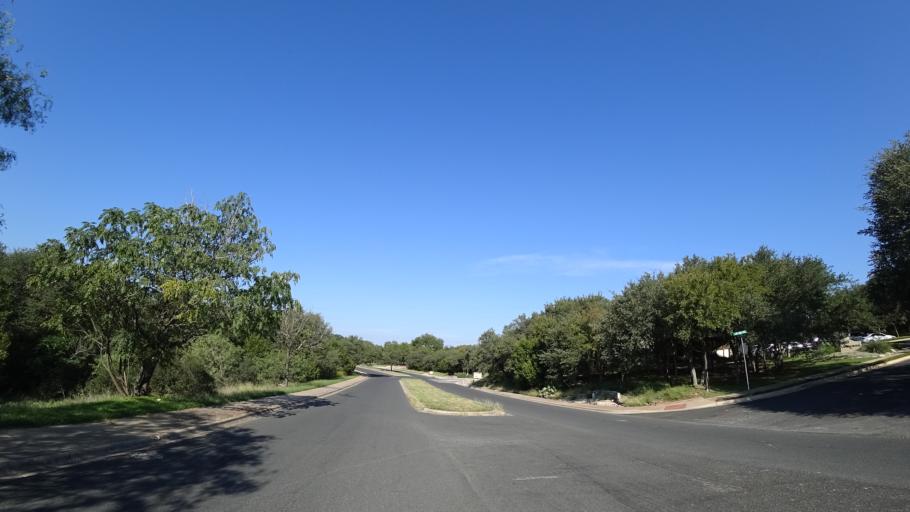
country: US
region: Texas
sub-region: Travis County
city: Rollingwood
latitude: 30.2658
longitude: -97.7886
